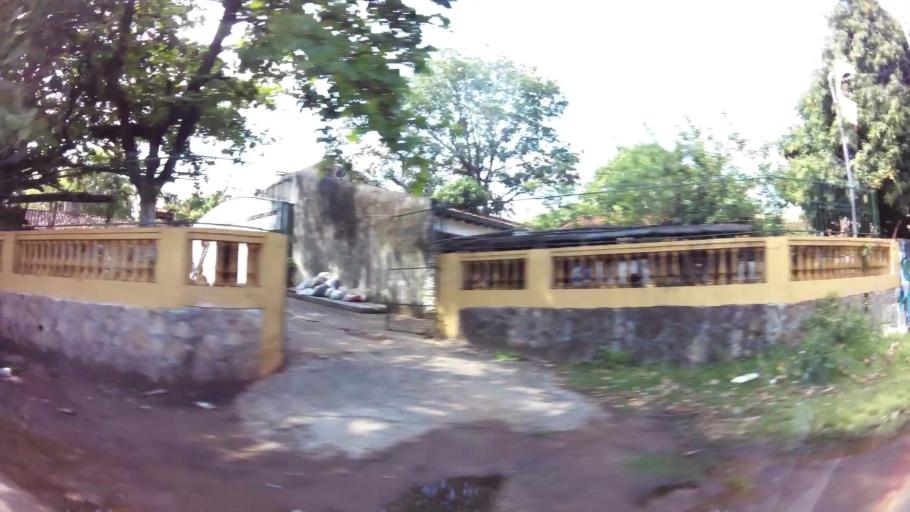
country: PY
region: Central
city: San Lorenzo
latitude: -25.2636
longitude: -57.4952
